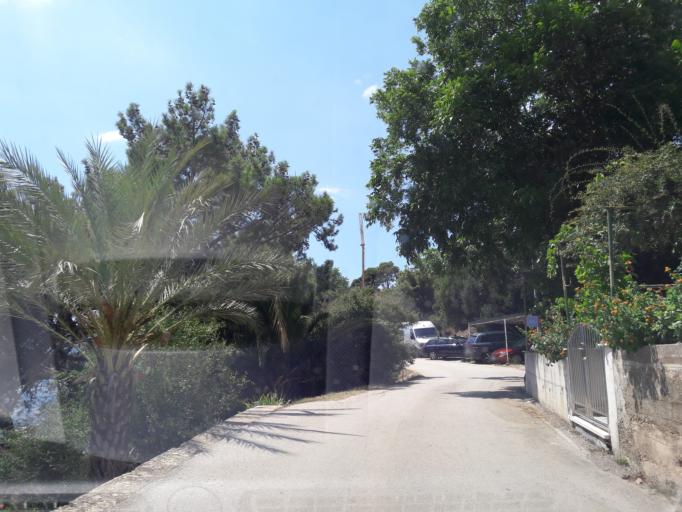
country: HR
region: Dubrovacko-Neretvanska
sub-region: Grad Korcula
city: Zrnovo
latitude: 42.9838
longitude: 17.0870
